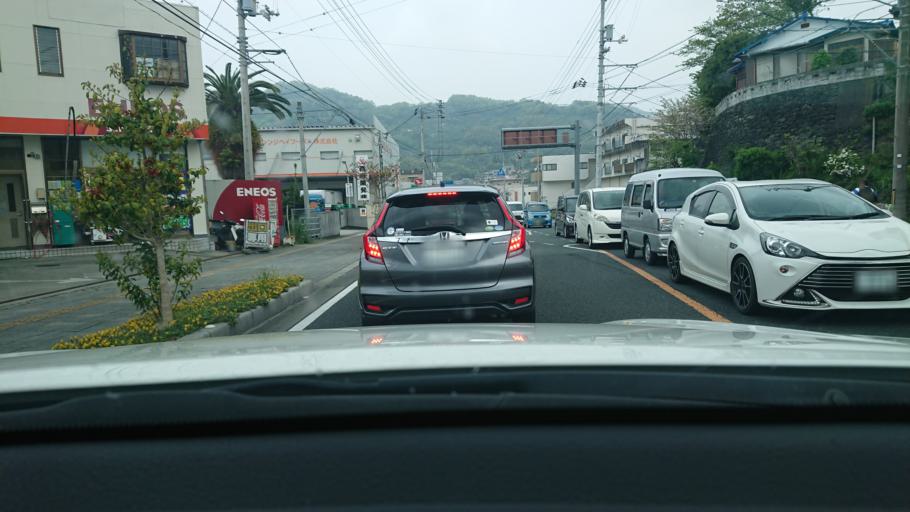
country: JP
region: Ehime
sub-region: Nishiuwa-gun
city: Ikata-cho
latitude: 33.4837
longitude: 132.4042
